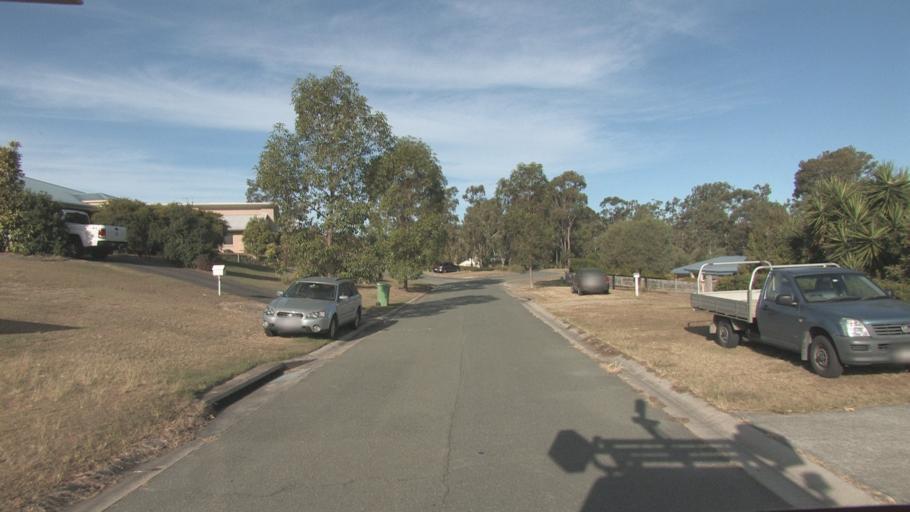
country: AU
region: Queensland
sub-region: Logan
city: North Maclean
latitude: -27.7999
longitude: 152.9596
